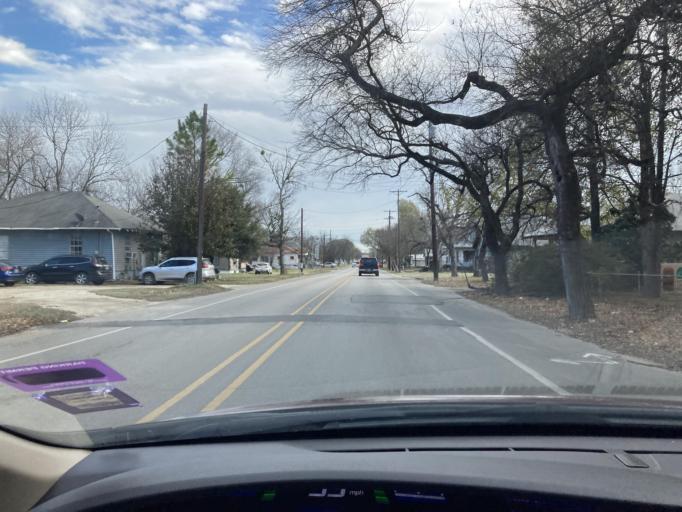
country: US
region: Texas
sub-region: Navarro County
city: Corsicana
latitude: 32.0869
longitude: -96.4663
